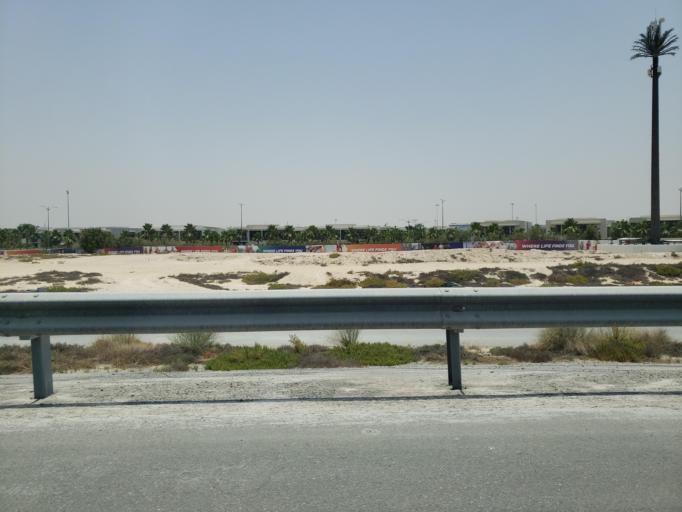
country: AE
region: Dubai
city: Dubai
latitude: 25.0290
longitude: 55.2492
